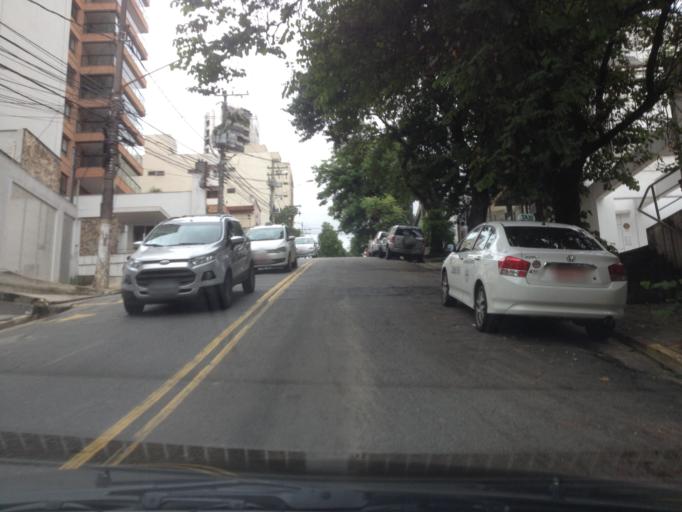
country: BR
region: Sao Paulo
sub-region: Sao Paulo
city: Sao Paulo
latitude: -23.5507
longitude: -46.6925
